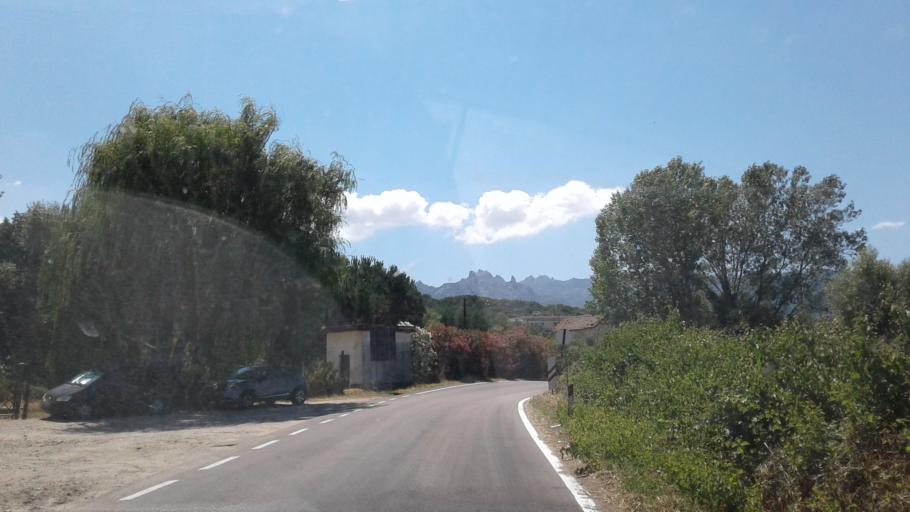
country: IT
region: Sardinia
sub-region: Provincia di Olbia-Tempio
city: Luras
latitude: 40.9241
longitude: 9.1791
